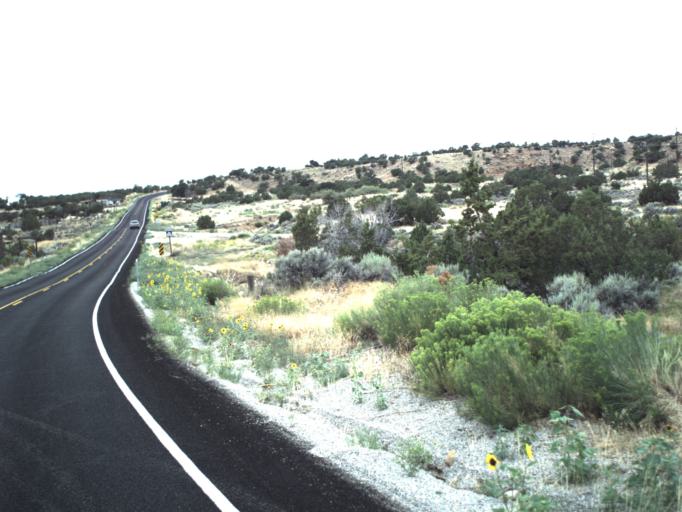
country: US
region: Utah
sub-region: Carbon County
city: East Carbon City
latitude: 39.5188
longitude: -110.3922
